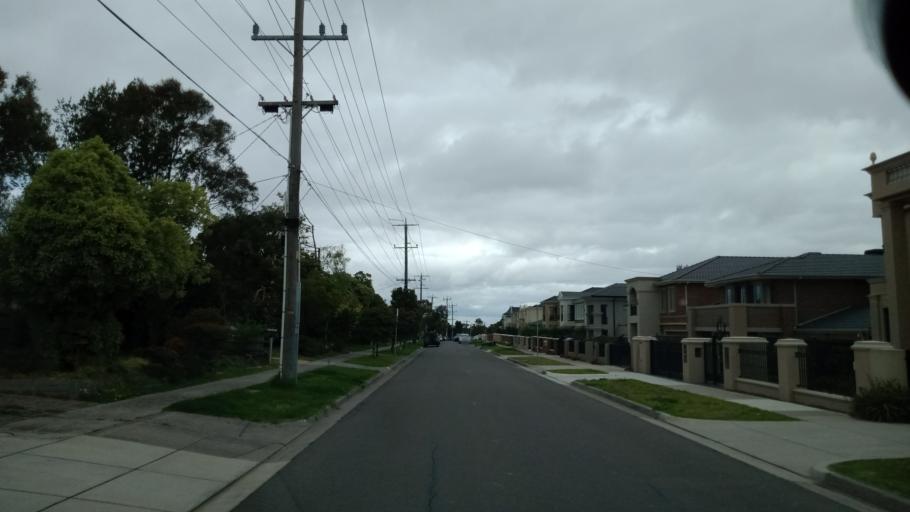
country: AU
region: Victoria
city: Burwood East
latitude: -37.8758
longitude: 145.1577
